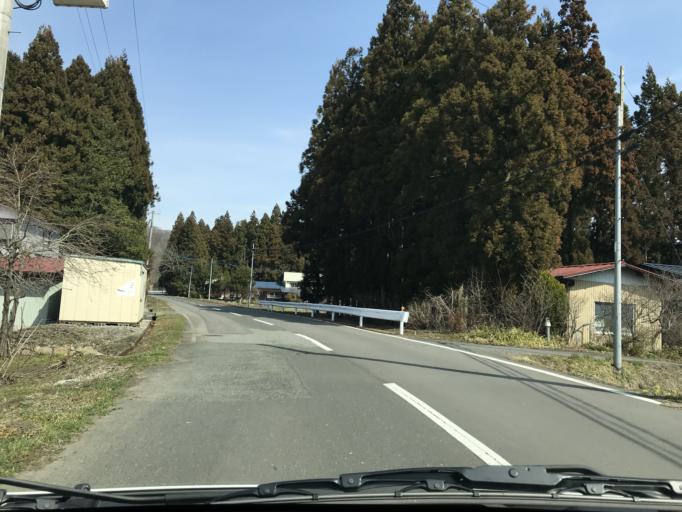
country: JP
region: Iwate
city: Mizusawa
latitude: 39.1244
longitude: 141.0147
